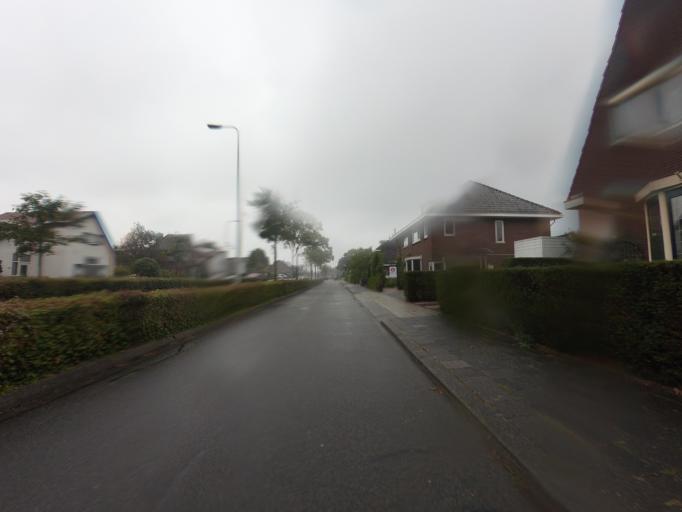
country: NL
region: Utrecht
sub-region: Gemeente IJsselstein
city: IJsselstein
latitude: 52.0795
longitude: 5.0355
